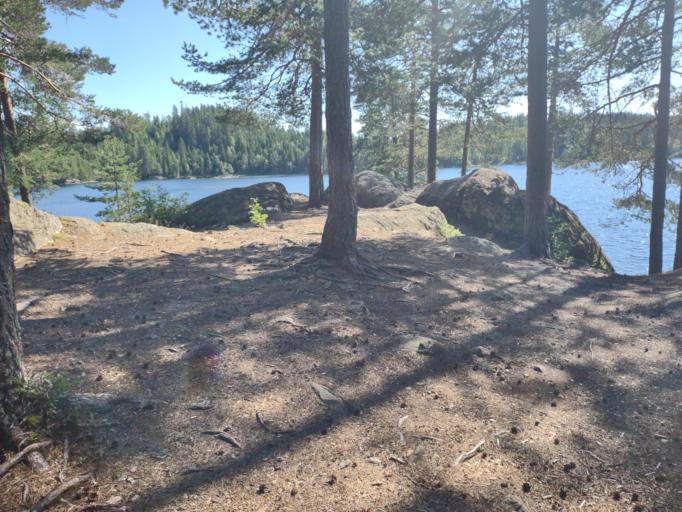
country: NO
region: Akershus
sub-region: Raelingen
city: Fjerdingby
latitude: 59.8896
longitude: 11.0598
